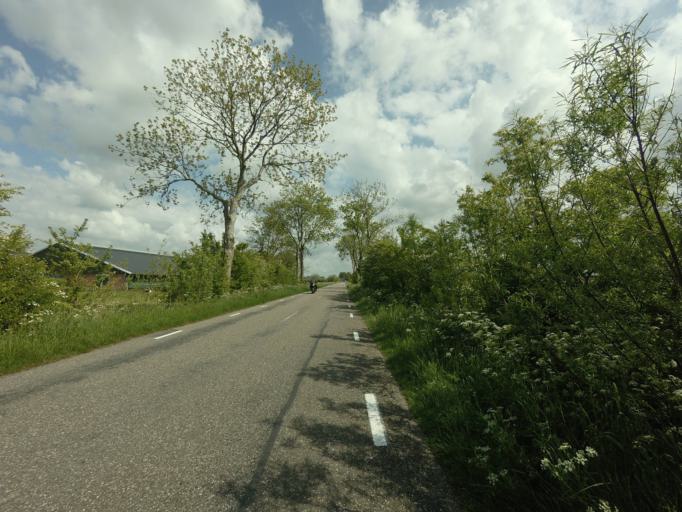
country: NL
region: Friesland
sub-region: Gemeente Littenseradiel
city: Makkum
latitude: 53.0979
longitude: 5.6515
